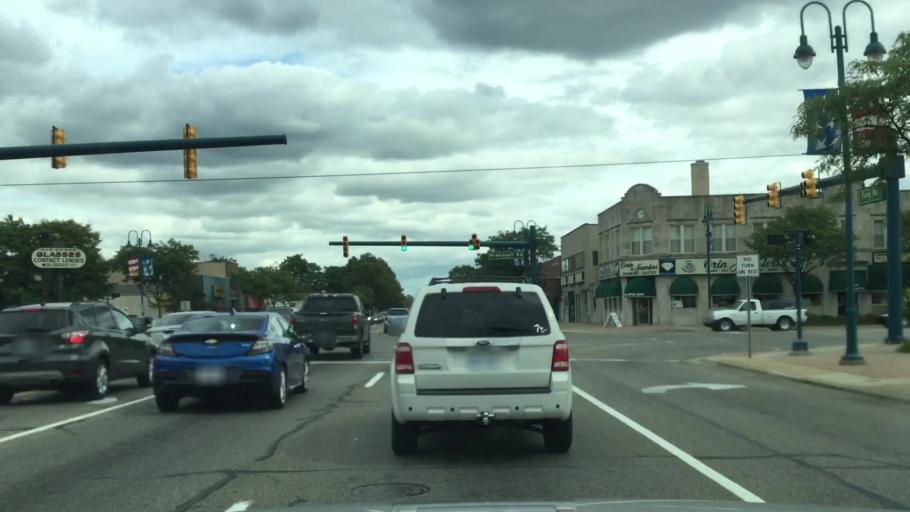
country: US
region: Michigan
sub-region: Wayne County
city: Garden City
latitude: 42.3259
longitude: -83.3296
